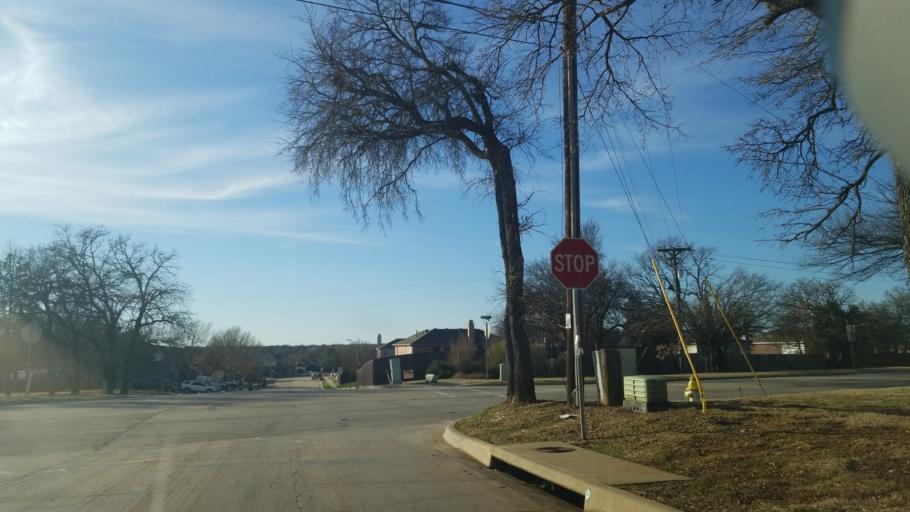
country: US
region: Texas
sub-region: Denton County
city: Corinth
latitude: 33.1360
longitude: -97.0642
